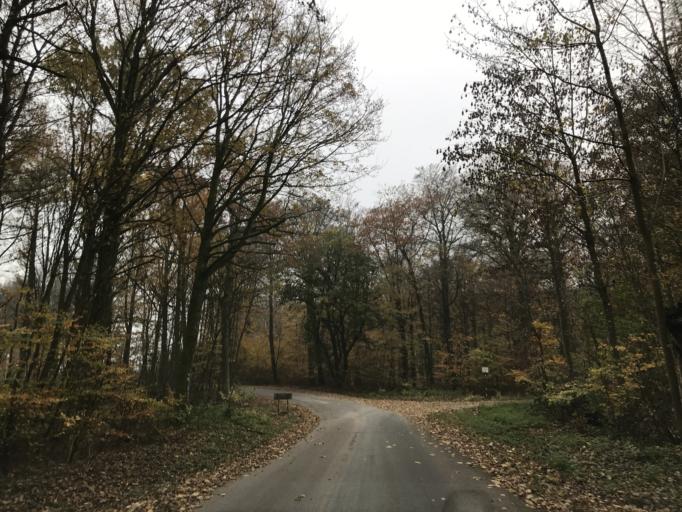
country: SE
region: Skane
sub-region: Klippans Kommun
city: Ljungbyhed
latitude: 55.9864
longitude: 13.2001
